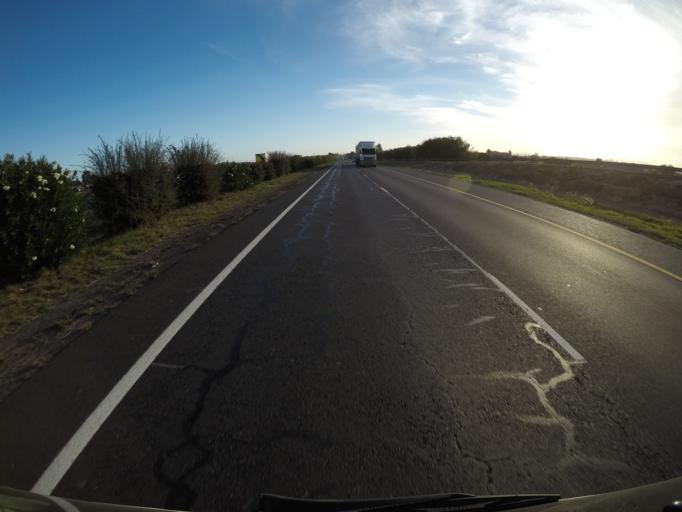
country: ZA
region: Western Cape
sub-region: City of Cape Town
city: Kraaifontein
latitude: -33.8456
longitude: 18.7144
